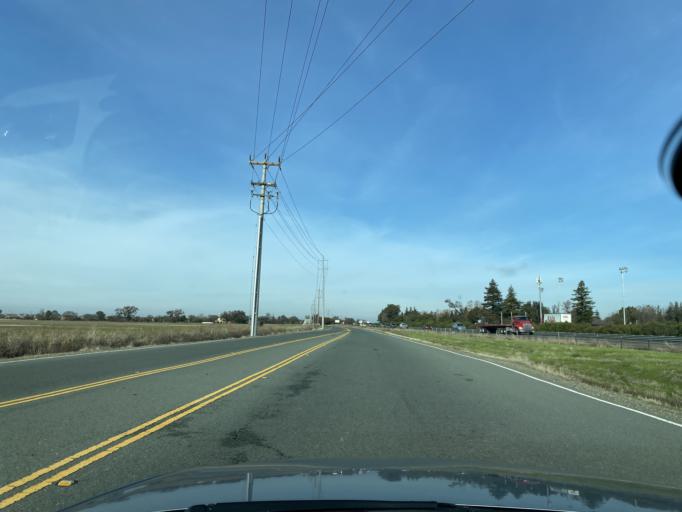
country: US
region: California
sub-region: Sacramento County
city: Elk Grove
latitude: 38.3876
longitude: -121.3737
